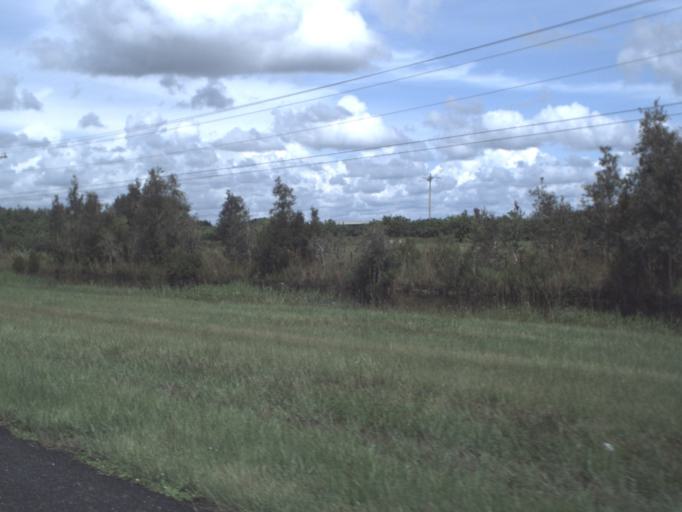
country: US
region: Florida
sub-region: Lee County
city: Suncoast Estates
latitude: 26.7831
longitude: -81.9395
